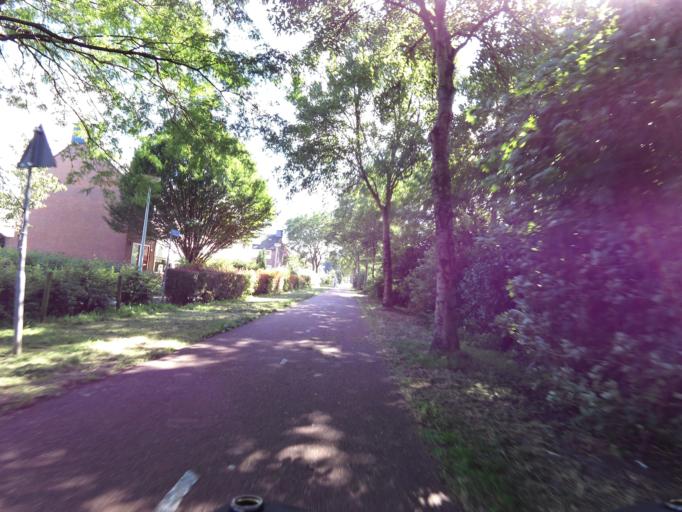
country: NL
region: South Holland
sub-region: Gemeente Barendrecht
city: Barendrecht
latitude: 51.8550
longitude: 4.5289
